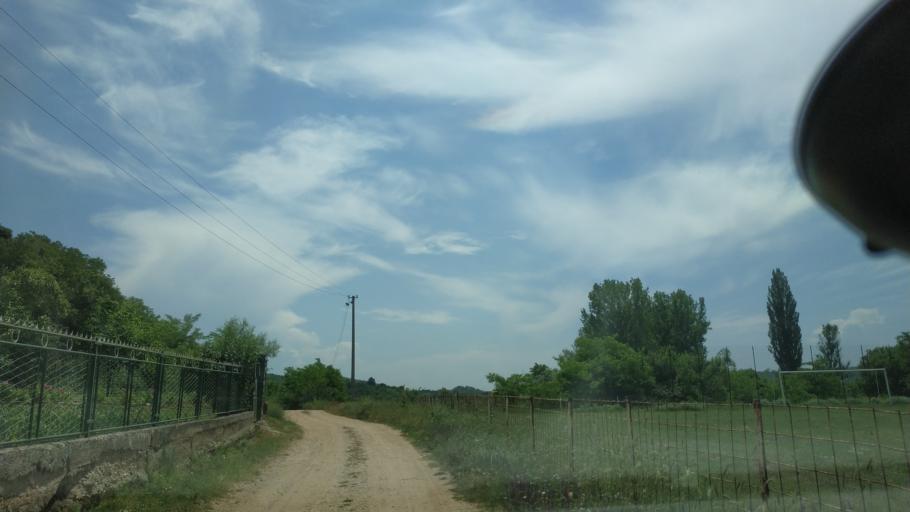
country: RS
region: Central Serbia
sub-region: Nisavski Okrug
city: Aleksinac
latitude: 43.5743
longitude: 21.7031
